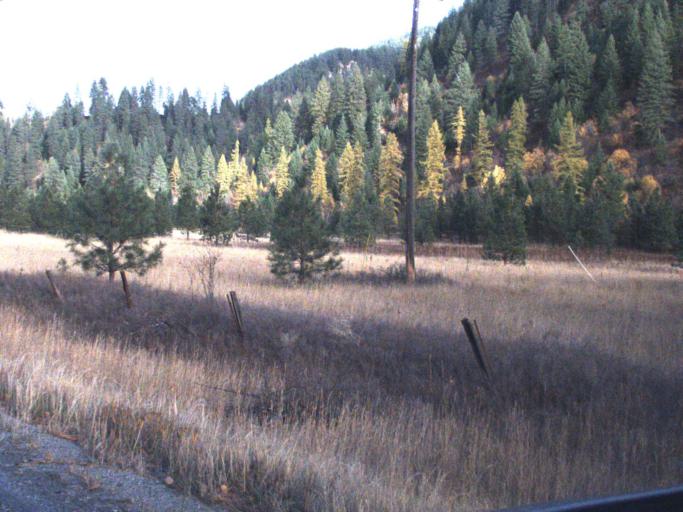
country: US
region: Washington
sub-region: Stevens County
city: Kettle Falls
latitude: 48.8272
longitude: -117.9113
